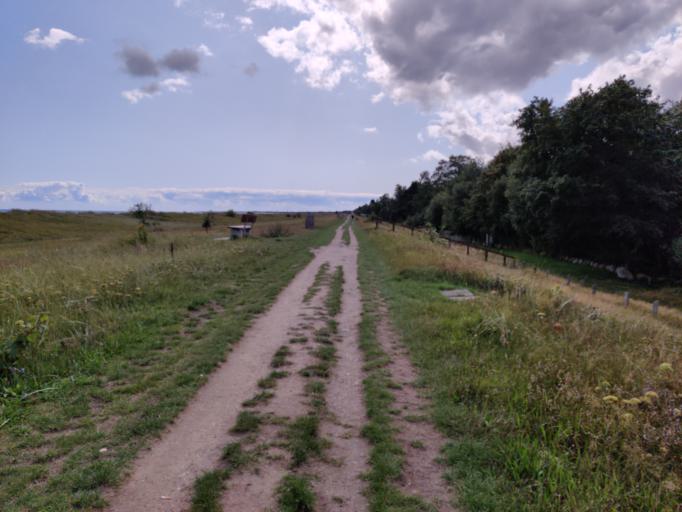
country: DK
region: Zealand
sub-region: Guldborgsund Kommune
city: Nykobing Falster
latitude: 54.6948
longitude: 11.9719
